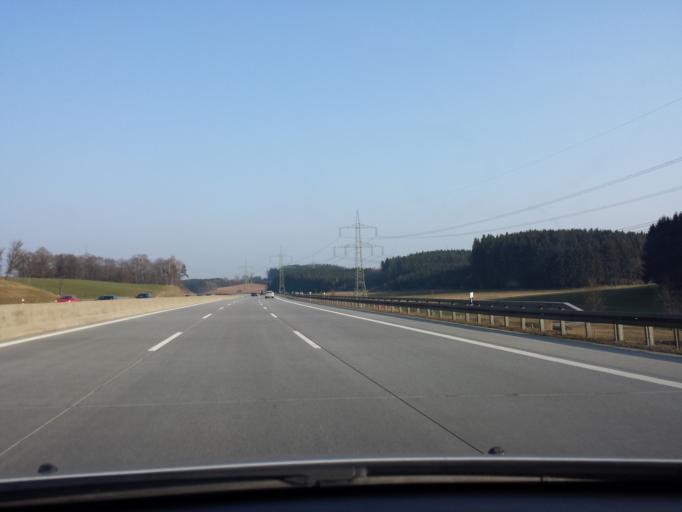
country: DE
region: Bavaria
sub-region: Swabia
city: Dasing
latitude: 48.3985
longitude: 11.0200
